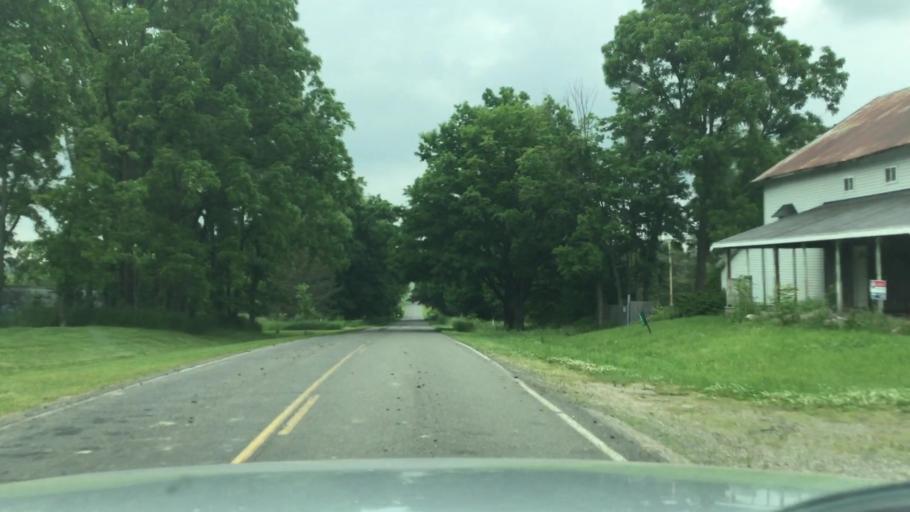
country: US
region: Michigan
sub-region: Shiawassee County
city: Durand
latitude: 42.7875
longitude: -84.0017
